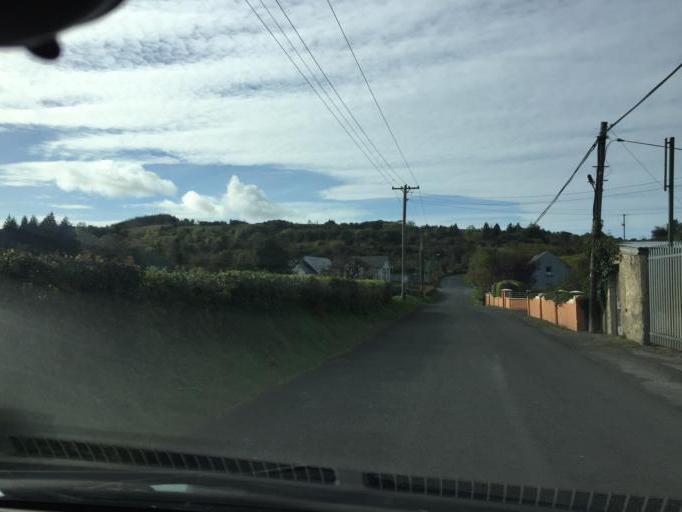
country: IE
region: Connaught
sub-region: Roscommon
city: Boyle
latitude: 54.0565
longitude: -8.2449
